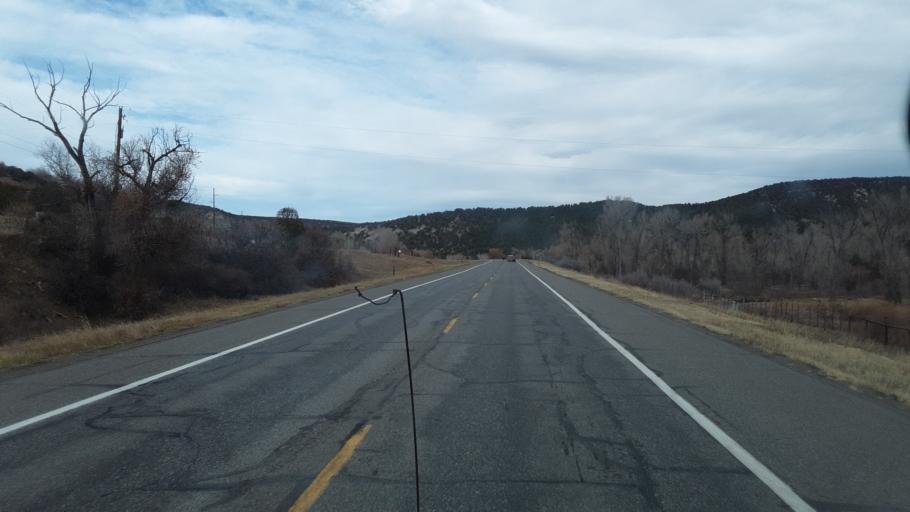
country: US
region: Colorado
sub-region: Ouray County
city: Ouray
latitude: 38.2365
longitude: -107.7372
